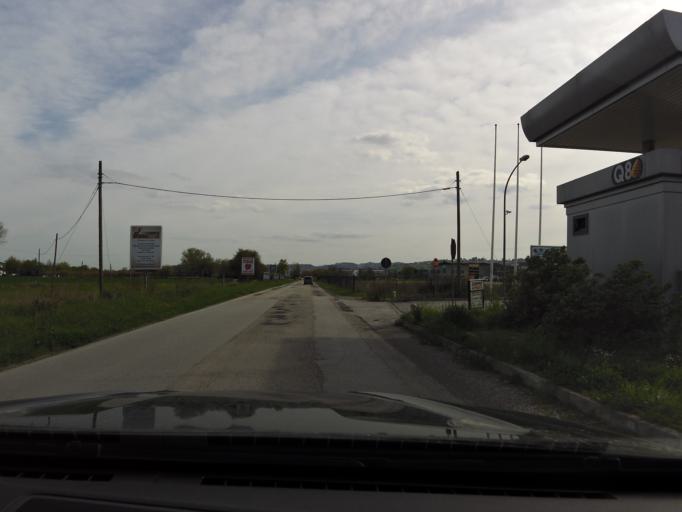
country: IT
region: The Marches
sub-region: Provincia di Ancona
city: Camerano
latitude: 43.5192
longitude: 13.5290
